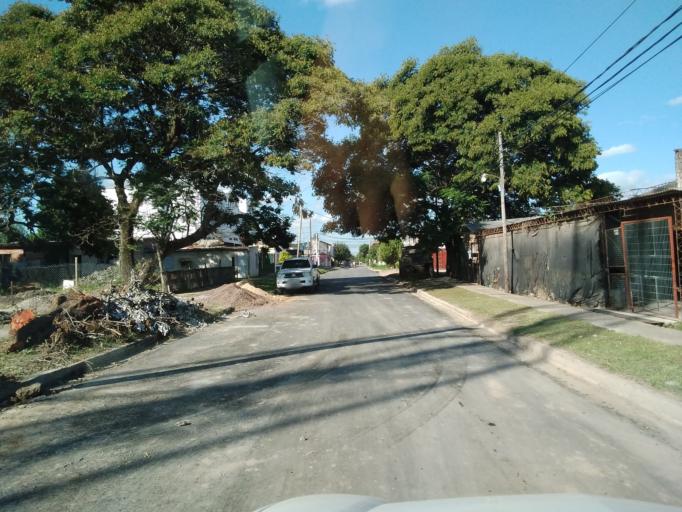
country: AR
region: Corrientes
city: Corrientes
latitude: -27.4642
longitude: -58.7867
